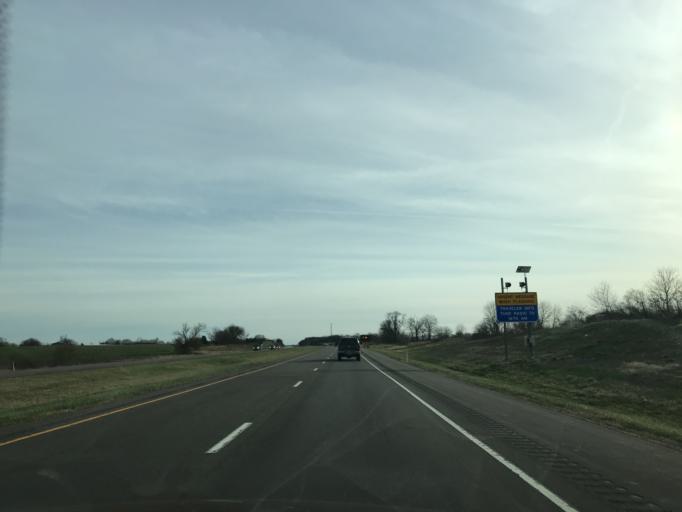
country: US
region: Pennsylvania
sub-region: Northumberland County
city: Watsontown
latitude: 41.0870
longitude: -76.8177
